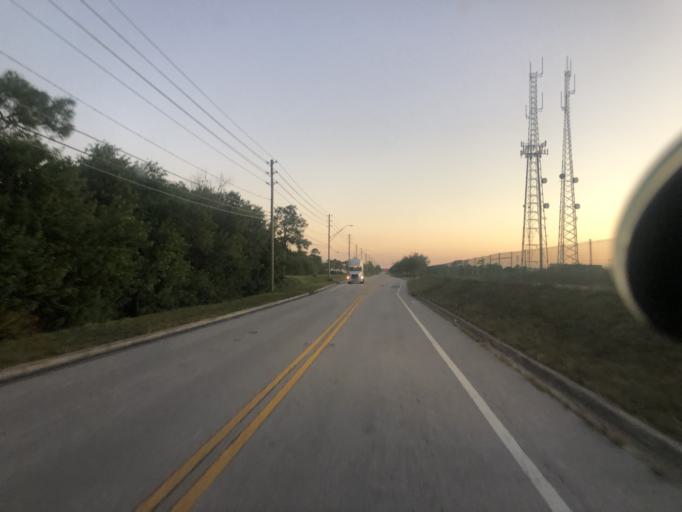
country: US
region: Florida
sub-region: Pinellas County
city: Gandy
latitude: 27.8697
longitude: -82.6553
